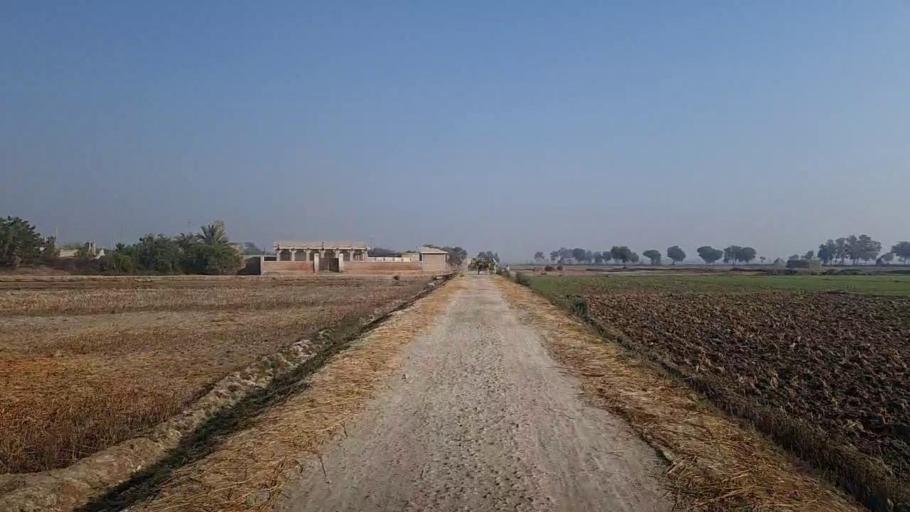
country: PK
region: Sindh
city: Radhan
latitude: 27.1172
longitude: 67.8955
